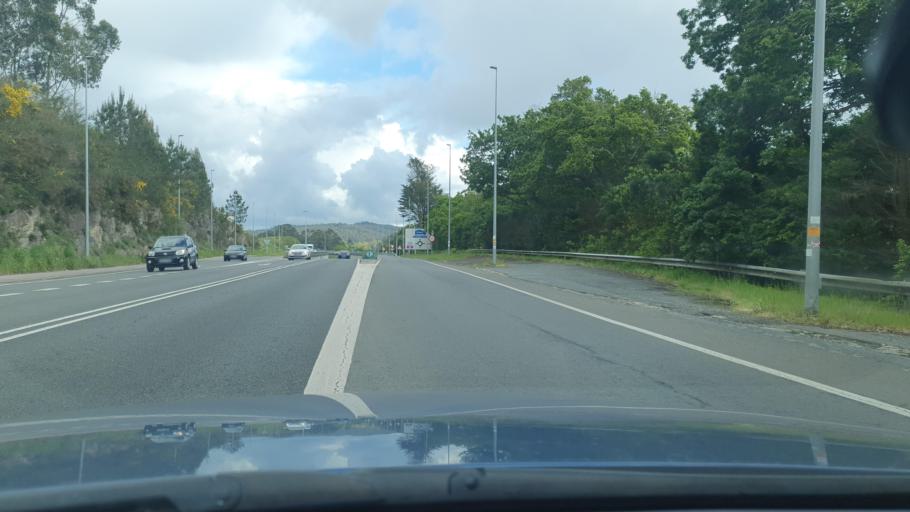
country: ES
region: Galicia
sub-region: Provincia da Coruna
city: Santiago de Compostela
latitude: 42.8713
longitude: -8.5787
